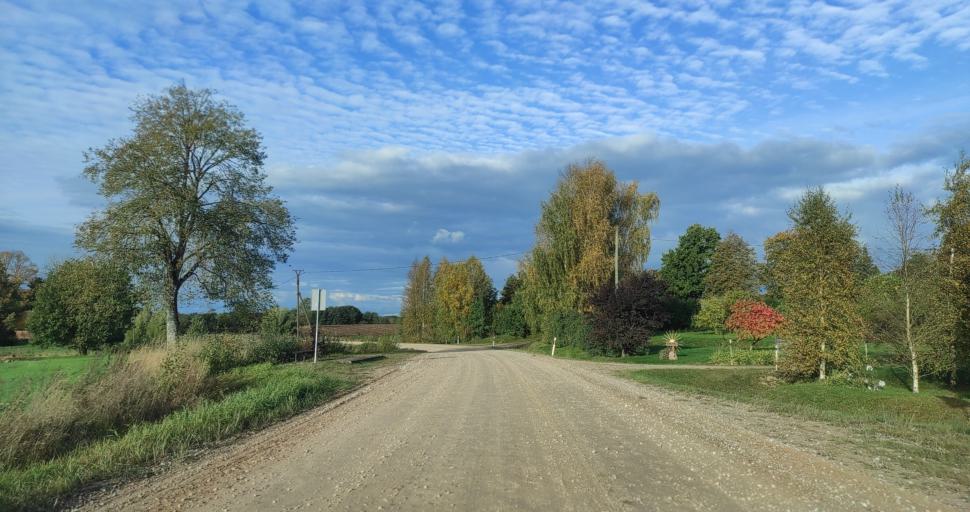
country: LV
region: Aizpute
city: Aizpute
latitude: 56.7494
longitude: 21.7996
